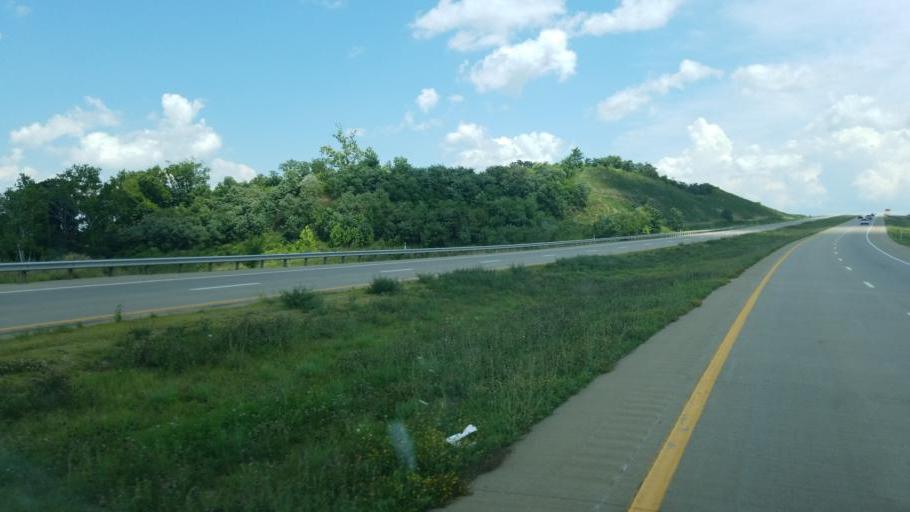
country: US
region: West Virginia
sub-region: Mason County
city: Point Pleasant
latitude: 38.7701
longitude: -82.0353
